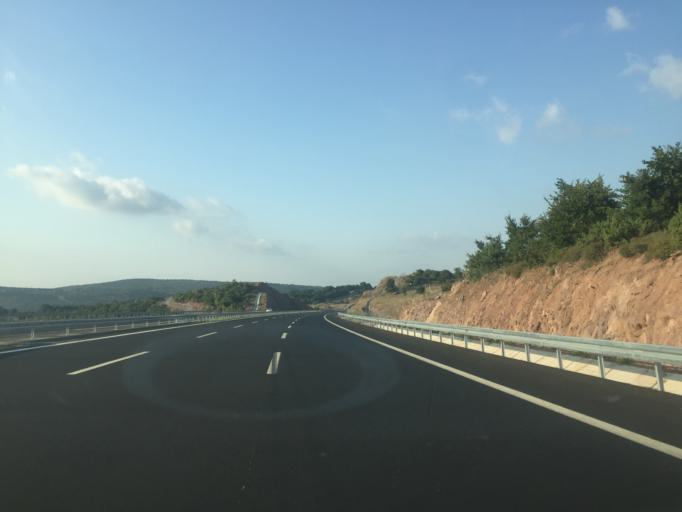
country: TR
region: Balikesir
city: Ertugrul
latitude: 39.5369
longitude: 27.6757
